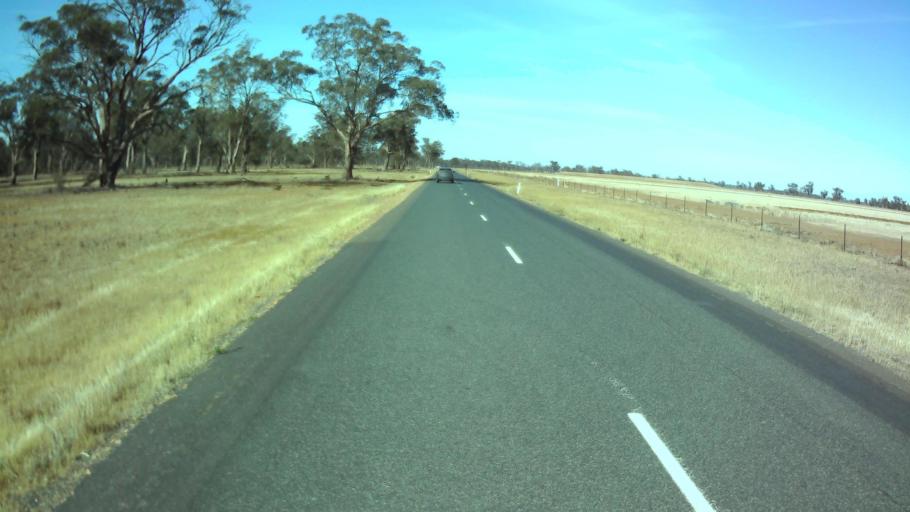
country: AU
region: New South Wales
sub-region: Weddin
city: Grenfell
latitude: -34.1238
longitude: 147.8067
